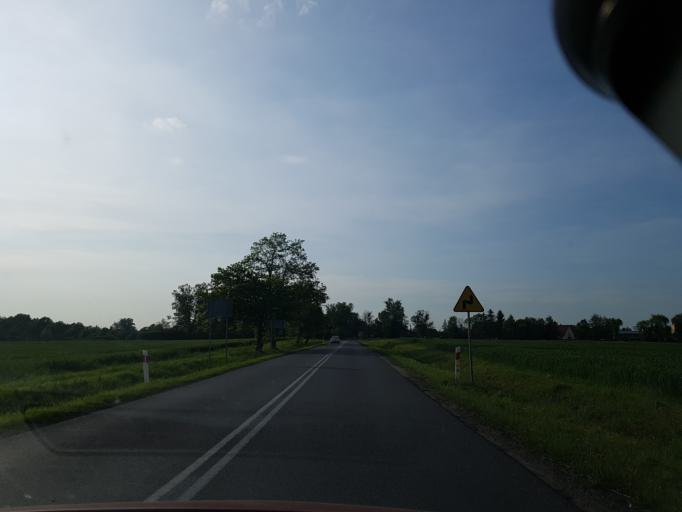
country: PL
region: Lower Silesian Voivodeship
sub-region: Powiat wroclawski
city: Gniechowice
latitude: 50.9799
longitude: 16.8502
